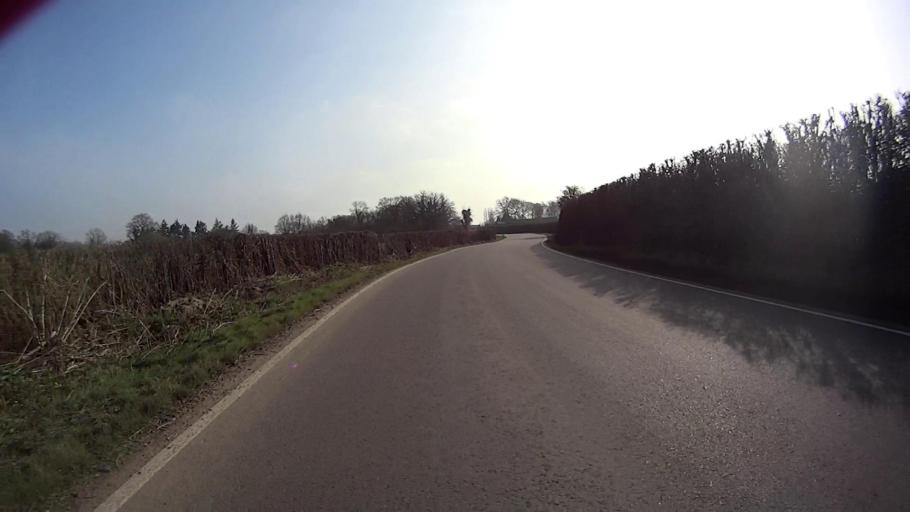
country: GB
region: England
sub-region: Surrey
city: Felbridge
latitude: 51.1786
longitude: -0.0659
